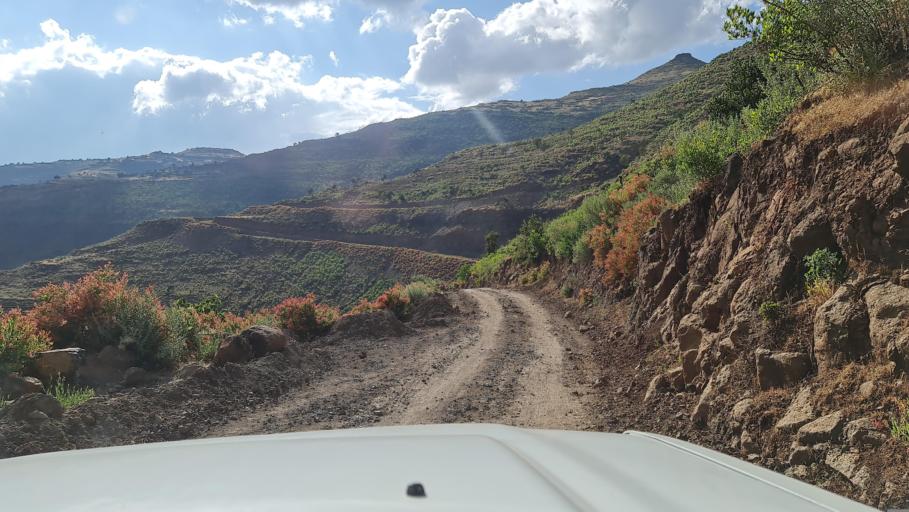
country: ET
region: Amhara
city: Debark'
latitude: 13.1209
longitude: 38.0205
